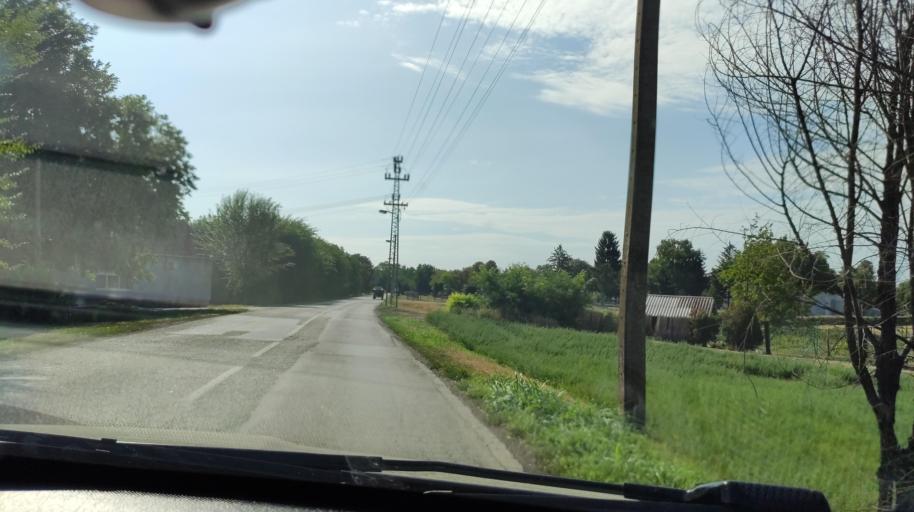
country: RS
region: Autonomna Pokrajina Vojvodina
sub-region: Severnobacki Okrug
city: Backa Topola
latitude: 45.8135
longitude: 19.6202
